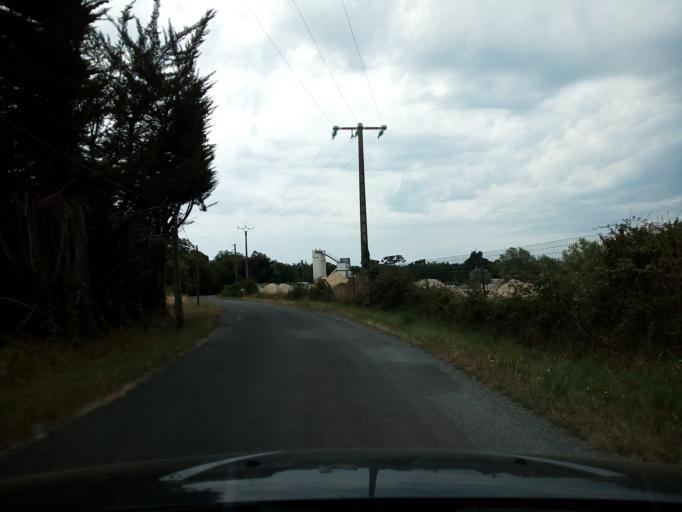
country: FR
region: Poitou-Charentes
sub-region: Departement de la Charente-Maritime
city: Dolus-d'Oleron
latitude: 45.9210
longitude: -1.2748
